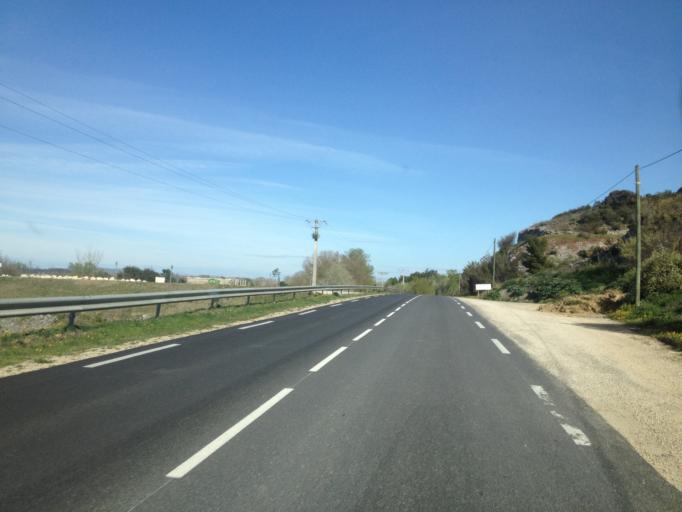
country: FR
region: Languedoc-Roussillon
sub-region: Departement du Gard
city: Roquemaure
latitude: 44.0668
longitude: 4.7905
